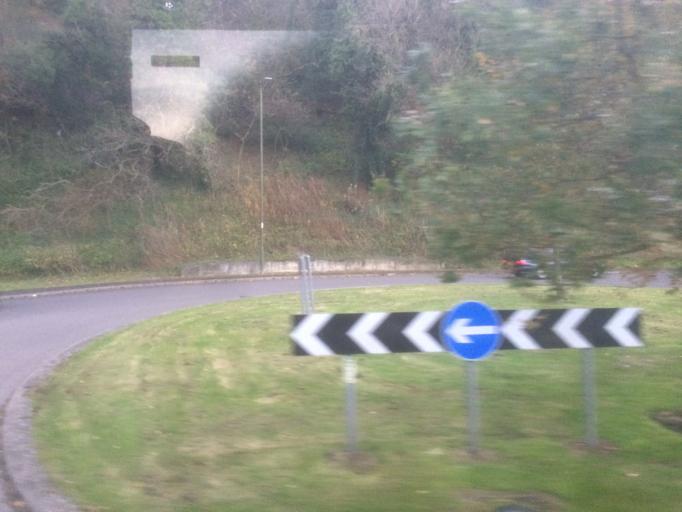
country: GB
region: Scotland
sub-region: Stirling
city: Stirling
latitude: 56.1267
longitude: -3.9493
